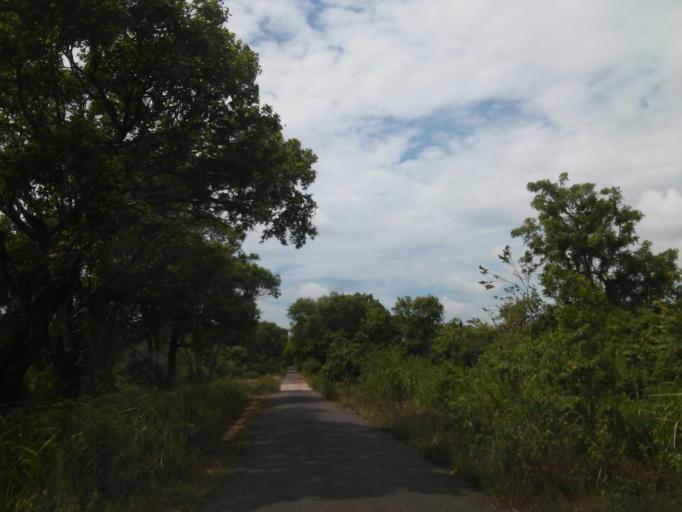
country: LK
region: Central
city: Sigiriya
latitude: 8.1007
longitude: 80.6803
